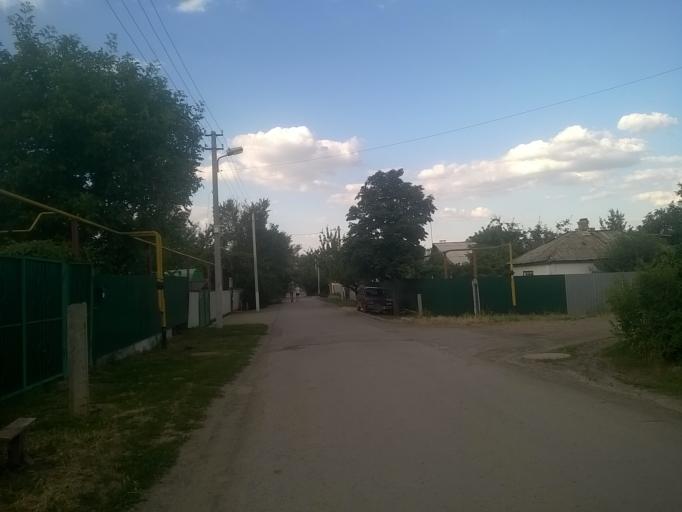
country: RU
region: Rostov
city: Donetsk
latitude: 48.3416
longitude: 39.9613
